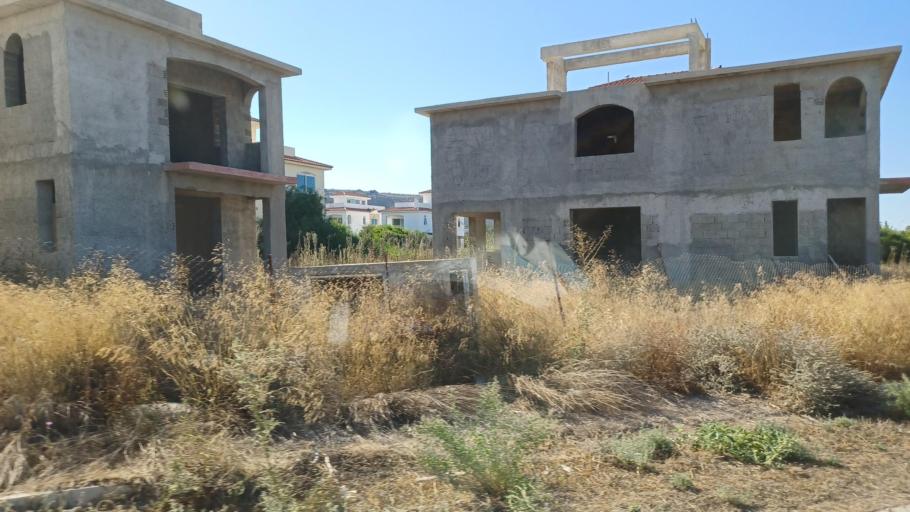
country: CY
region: Larnaka
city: Pyla
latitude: 34.9936
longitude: 33.6925
